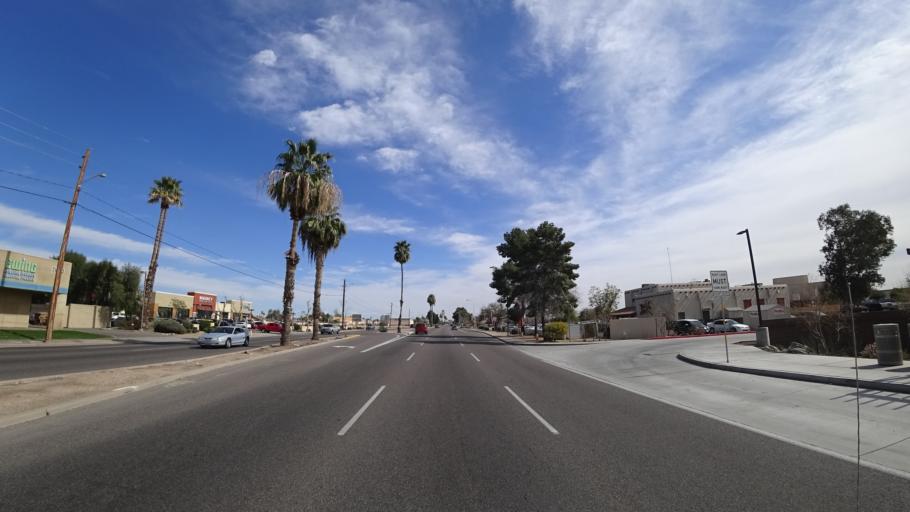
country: US
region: Arizona
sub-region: Maricopa County
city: Tolleson
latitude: 33.4799
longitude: -112.2286
